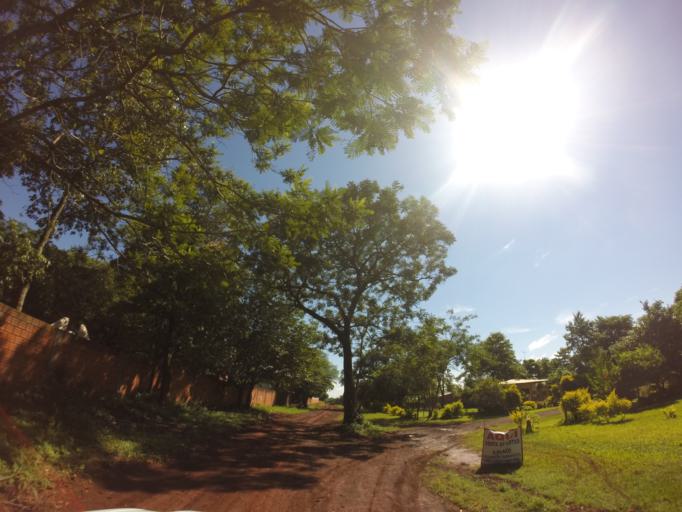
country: PY
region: Alto Parana
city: Ciudad del Este
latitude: -25.4217
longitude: -54.6481
